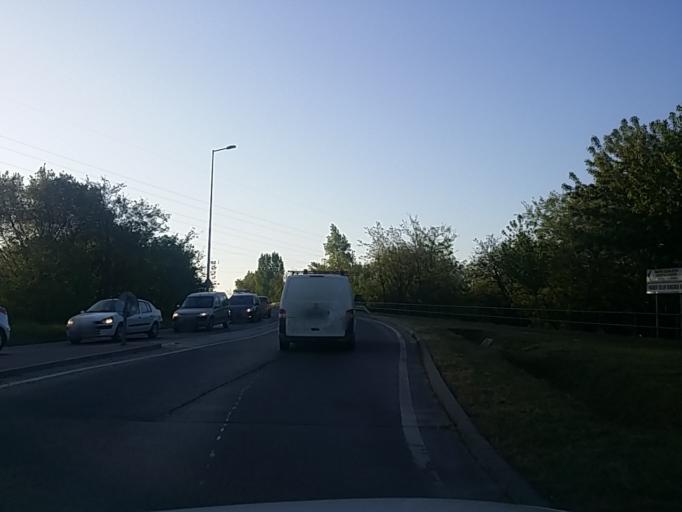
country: HU
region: Pest
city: Fot
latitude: 47.6186
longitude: 19.1664
